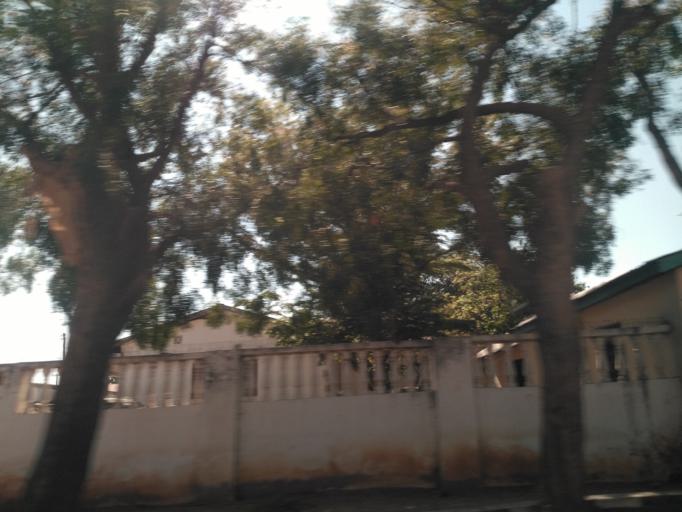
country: TZ
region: Dodoma
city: Dodoma
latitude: -6.1670
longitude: 35.7452
